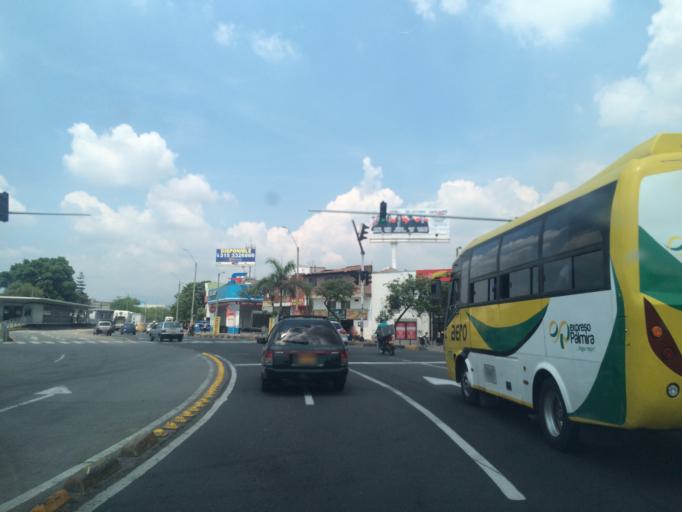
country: CO
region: Valle del Cauca
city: Cali
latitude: 3.4706
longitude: -76.5102
